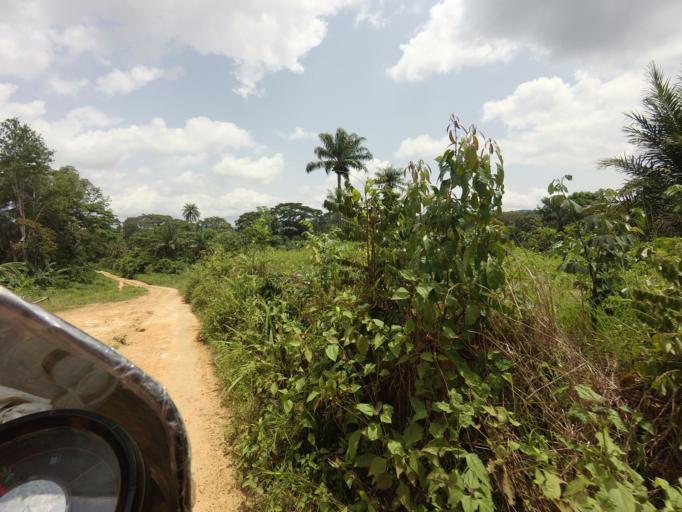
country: SL
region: Eastern Province
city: Kailahun
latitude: 8.3705
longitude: -10.7134
